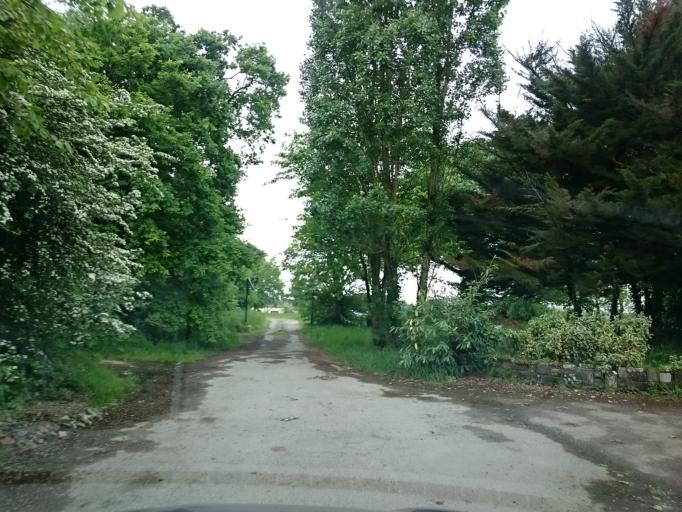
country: FR
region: Brittany
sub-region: Departement d'Ille-et-Vilaine
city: Vern-sur-Seiche
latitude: 48.0624
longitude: -1.6201
